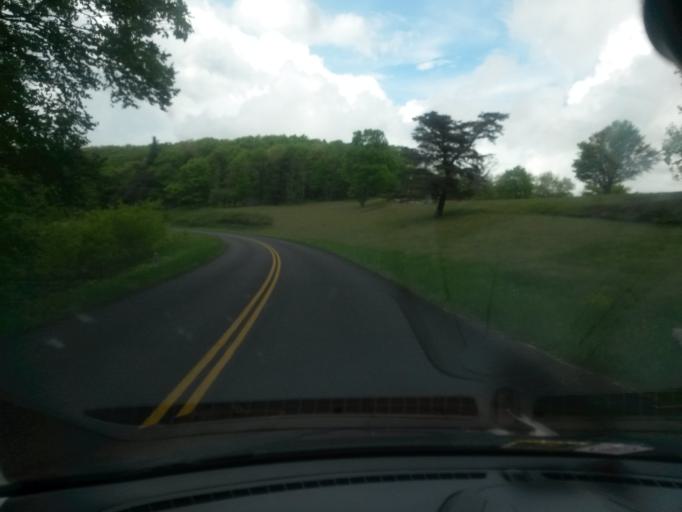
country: US
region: Virginia
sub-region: Floyd County
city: Floyd
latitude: 36.8222
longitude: -80.3425
